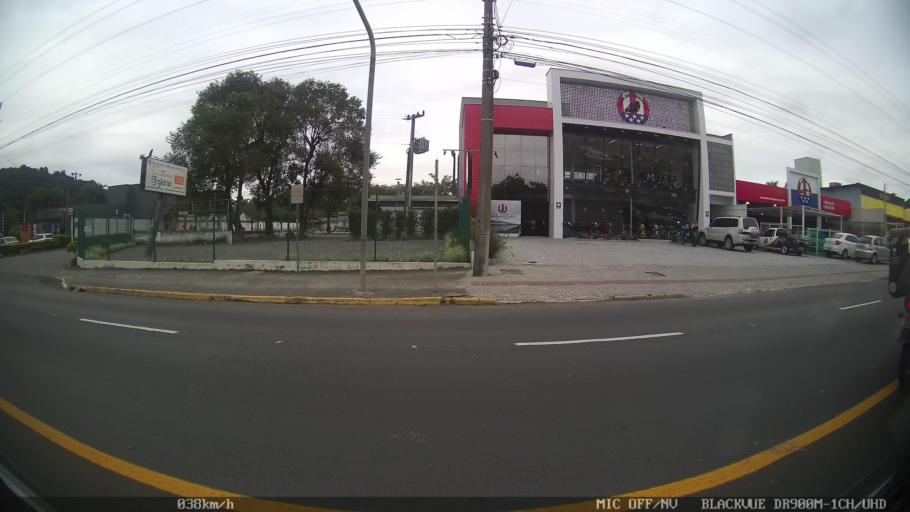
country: BR
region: Santa Catarina
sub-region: Joinville
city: Joinville
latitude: -26.2951
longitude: -48.8648
